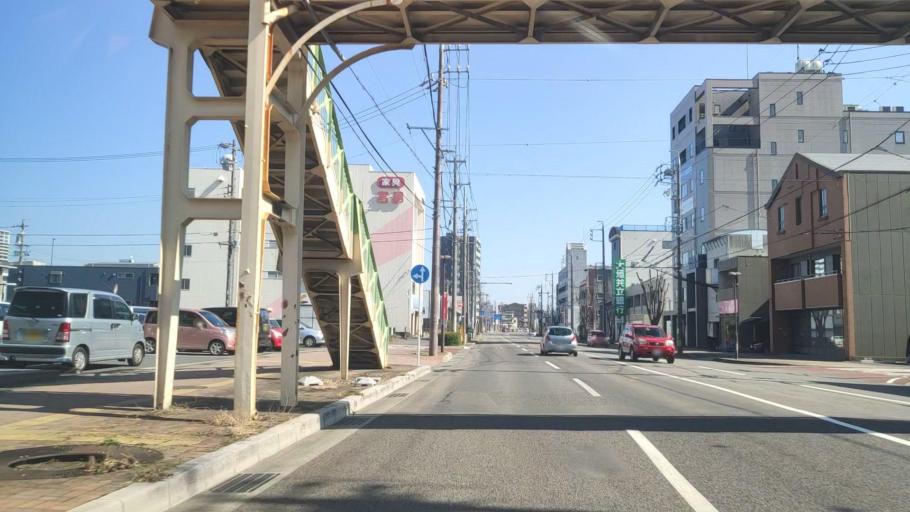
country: JP
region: Gifu
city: Gifu-shi
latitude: 35.4066
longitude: 136.7513
